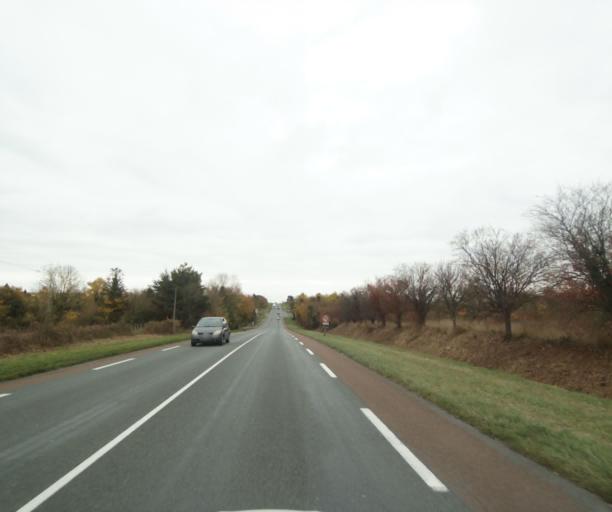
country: FR
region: Poitou-Charentes
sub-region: Departement de la Charente-Maritime
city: Les Gonds
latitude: 45.7157
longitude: -0.6340
